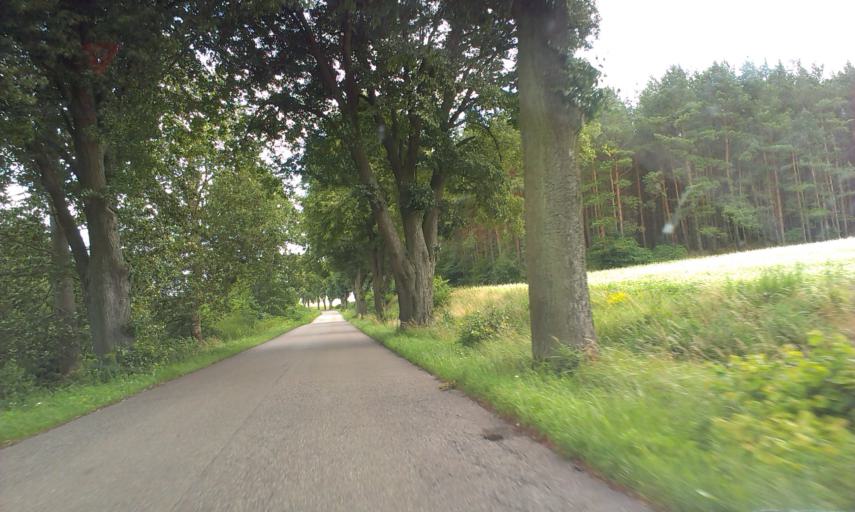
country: PL
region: Greater Poland Voivodeship
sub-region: Powiat zlotowski
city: Zlotow
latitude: 53.3935
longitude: 17.0014
